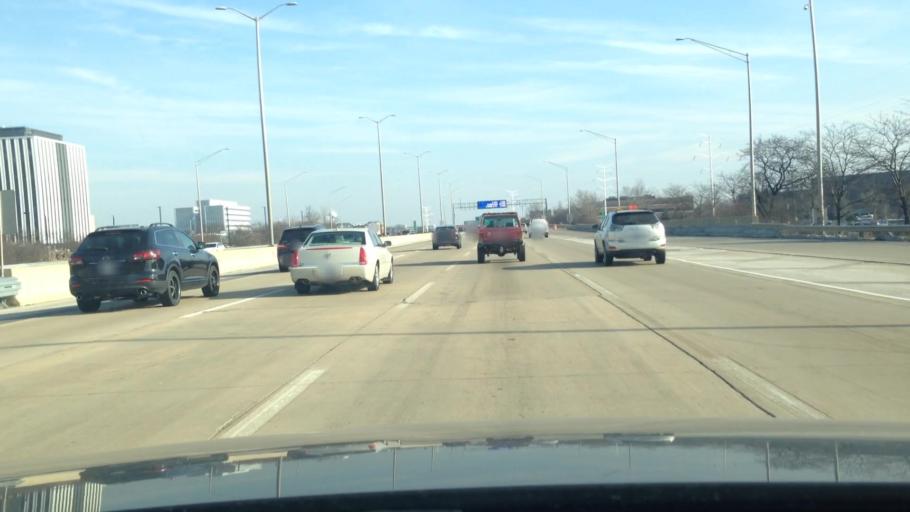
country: US
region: Illinois
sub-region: DuPage County
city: Oakbrook Terrace
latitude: 41.8446
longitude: -87.9534
